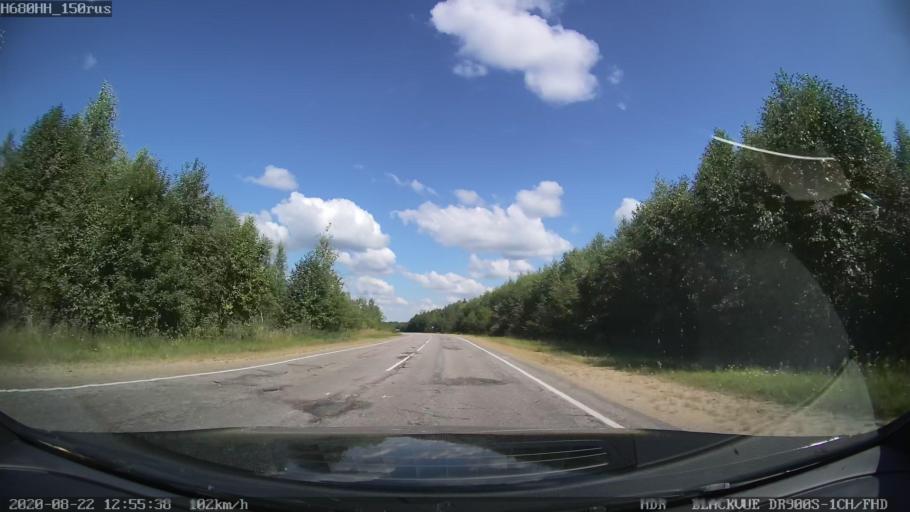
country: RU
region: Tverskaya
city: Rameshki
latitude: 57.5452
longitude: 36.3055
